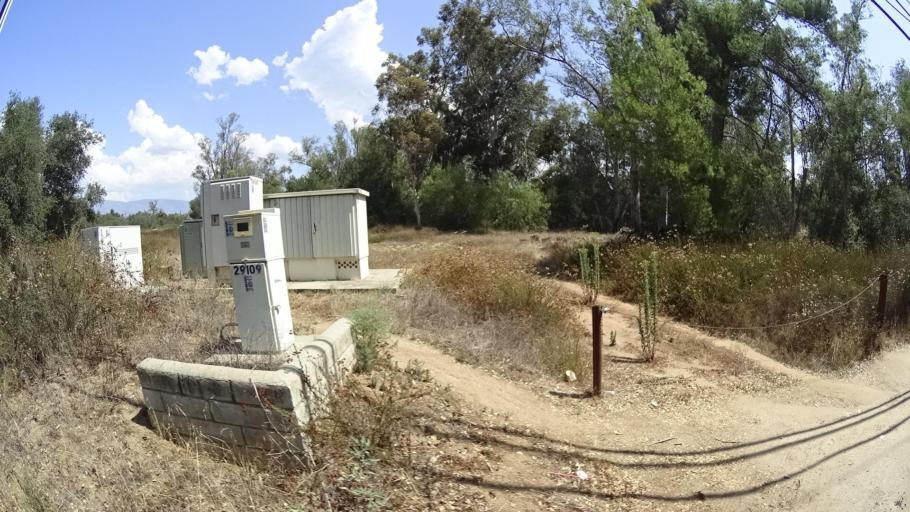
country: US
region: California
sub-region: San Diego County
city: Valley Center
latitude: 33.2436
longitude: -116.9932
